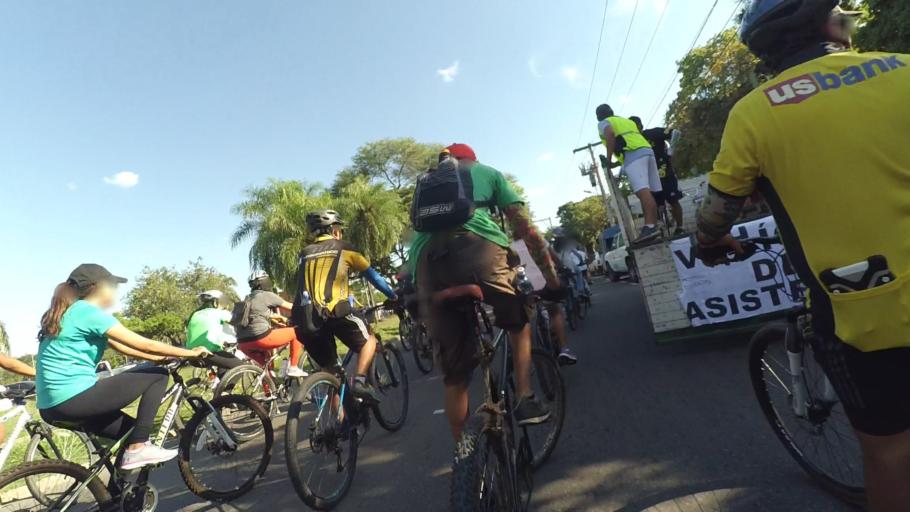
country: BO
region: Santa Cruz
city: Santa Cruz de la Sierra
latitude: -17.7930
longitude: -63.1746
